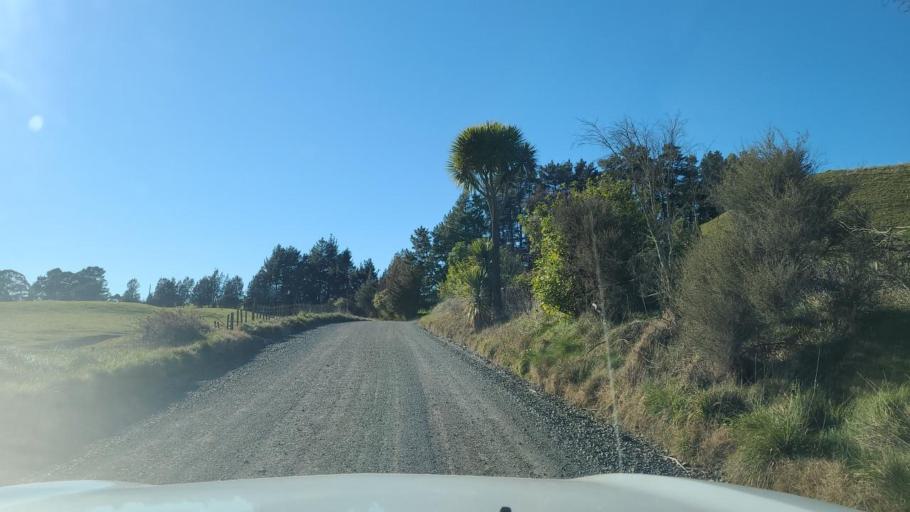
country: NZ
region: Hawke's Bay
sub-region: Napier City
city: Taradale
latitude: -39.3770
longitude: 176.5779
